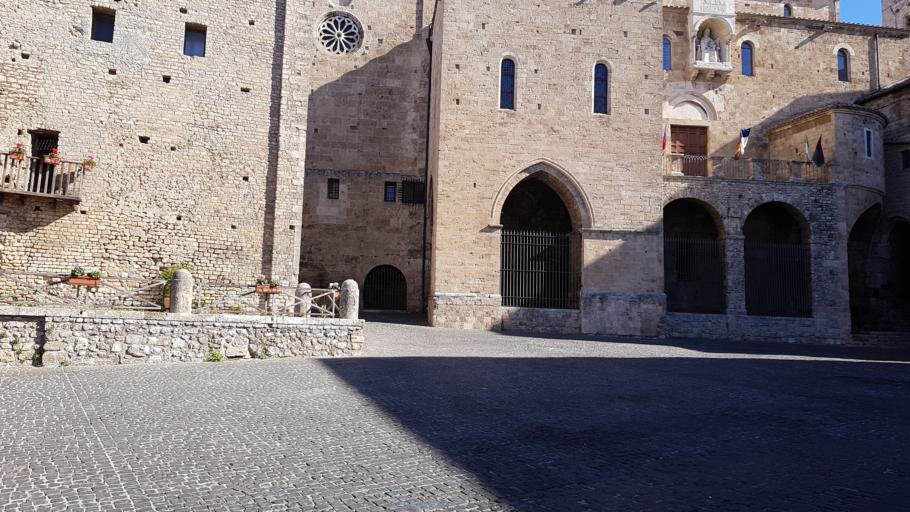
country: IT
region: Latium
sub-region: Provincia di Frosinone
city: Anagni
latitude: 41.7427
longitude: 13.1614
